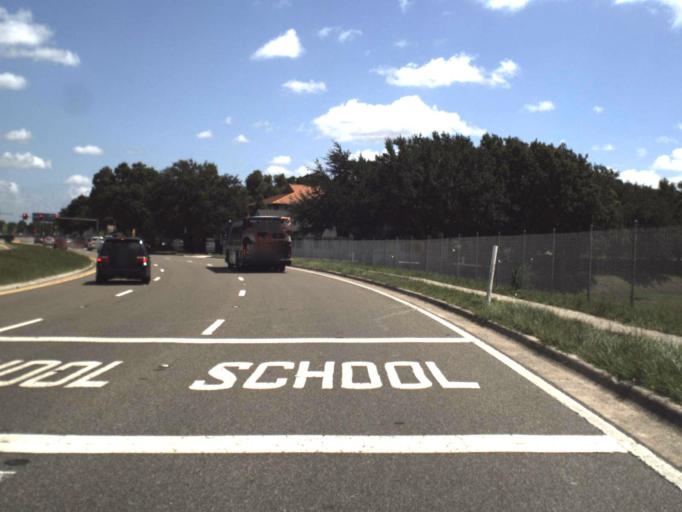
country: US
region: Florida
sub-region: Pinellas County
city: Safety Harbor
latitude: 28.0197
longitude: -82.7131
